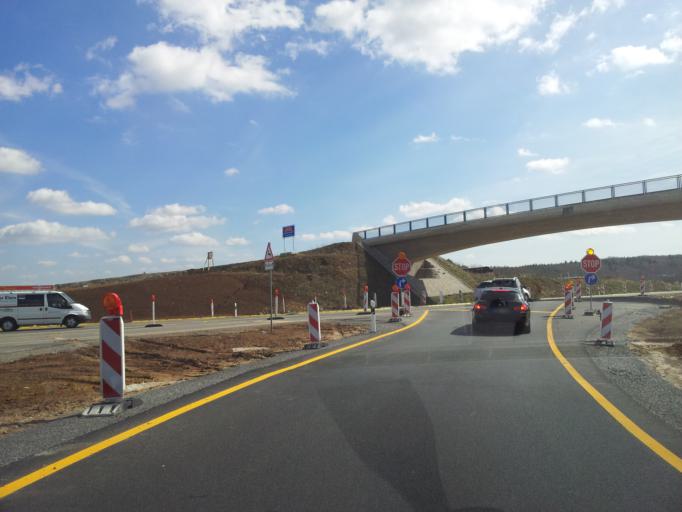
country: DE
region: Bavaria
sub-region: Regierungsbezirk Unterfranken
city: Reichenberg
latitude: 49.7511
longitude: 9.9274
